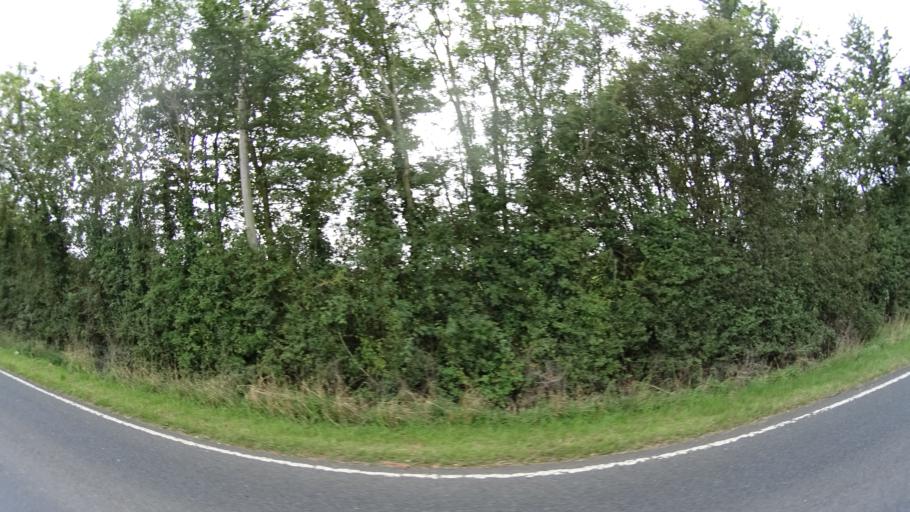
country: GB
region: England
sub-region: Dorset
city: Shaftesbury
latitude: 51.0165
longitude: -2.2313
